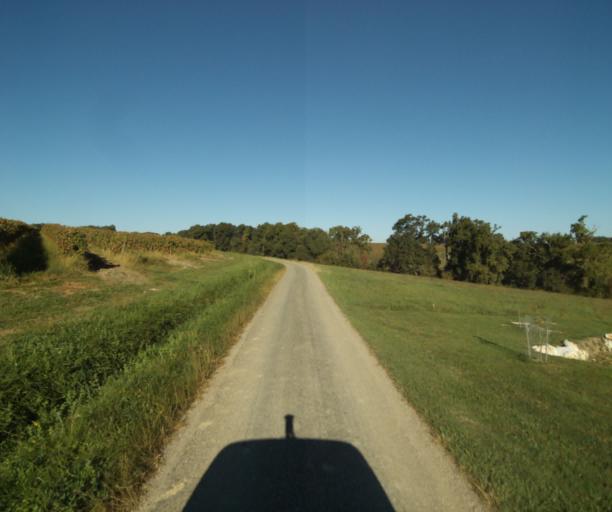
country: FR
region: Midi-Pyrenees
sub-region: Departement du Gers
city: Gondrin
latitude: 43.8367
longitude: 0.2803
